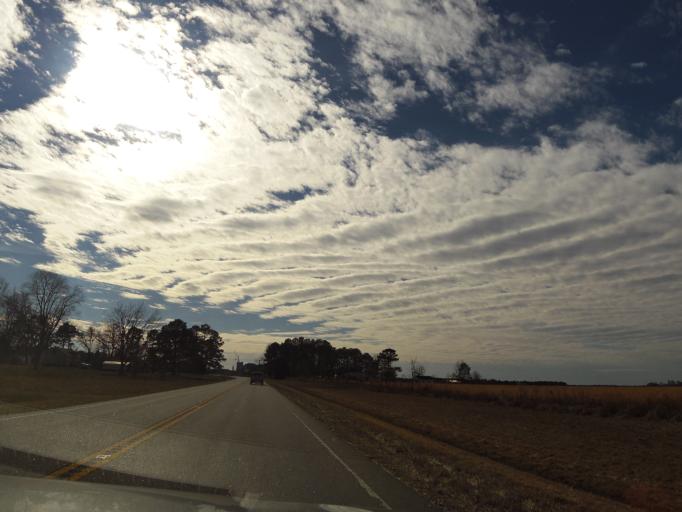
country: US
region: Virginia
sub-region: City of Franklin
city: Franklin
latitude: 36.7017
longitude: -76.8895
